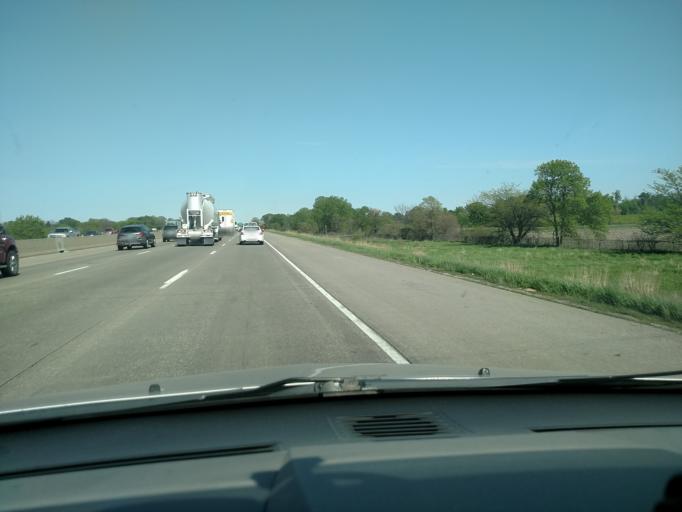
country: US
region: Iowa
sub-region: Polk County
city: Saylorville
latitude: 41.6494
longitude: -93.6379
